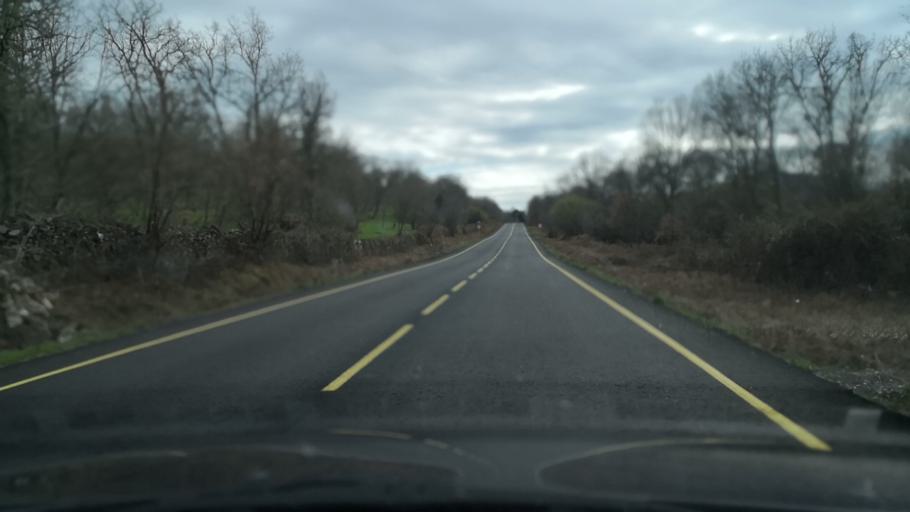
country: ES
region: Castille and Leon
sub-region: Provincia de Salamanca
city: Penaparda
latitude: 40.2691
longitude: -6.6867
